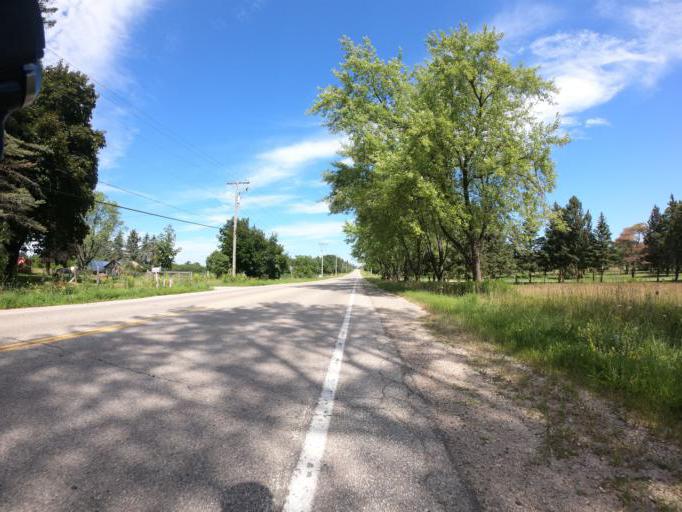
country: CA
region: Ontario
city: Waterloo
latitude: 43.5135
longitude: -80.3936
